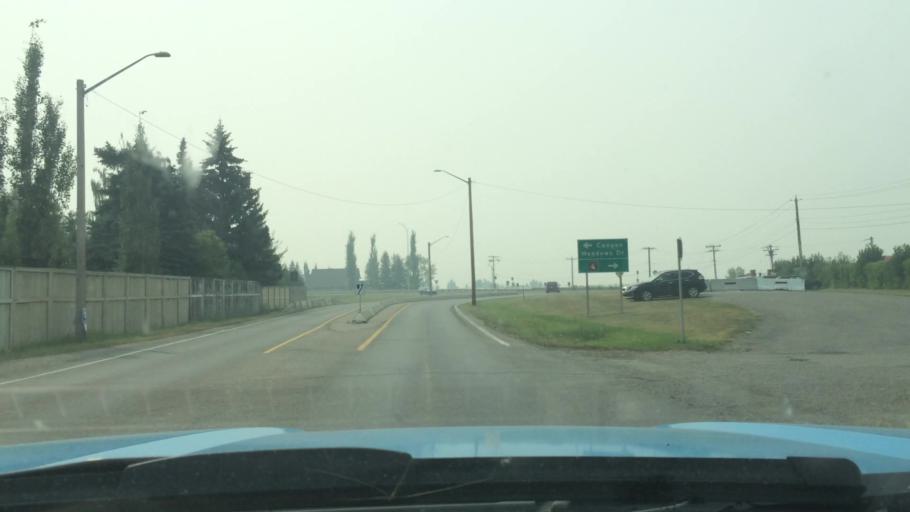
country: CA
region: Alberta
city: Calgary
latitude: 50.9417
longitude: -114.0945
